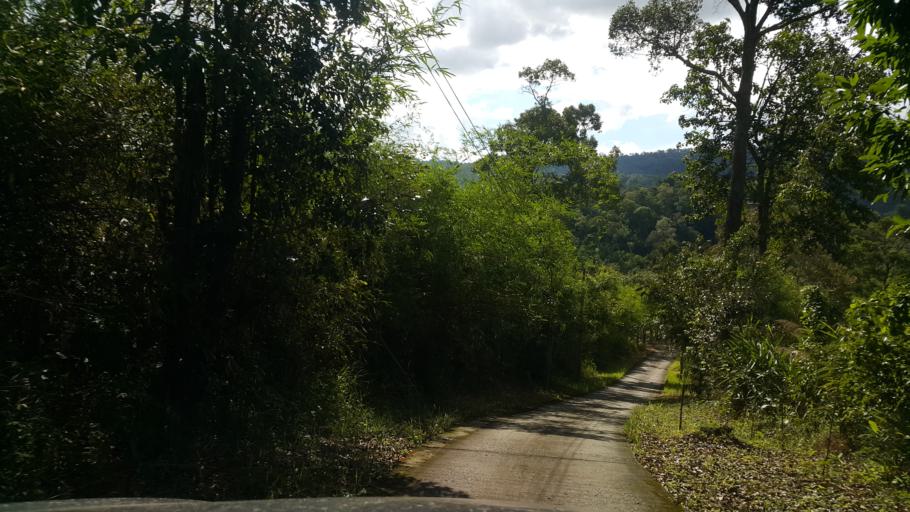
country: TH
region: Loei
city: Na Haeo
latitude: 17.5627
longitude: 100.9509
